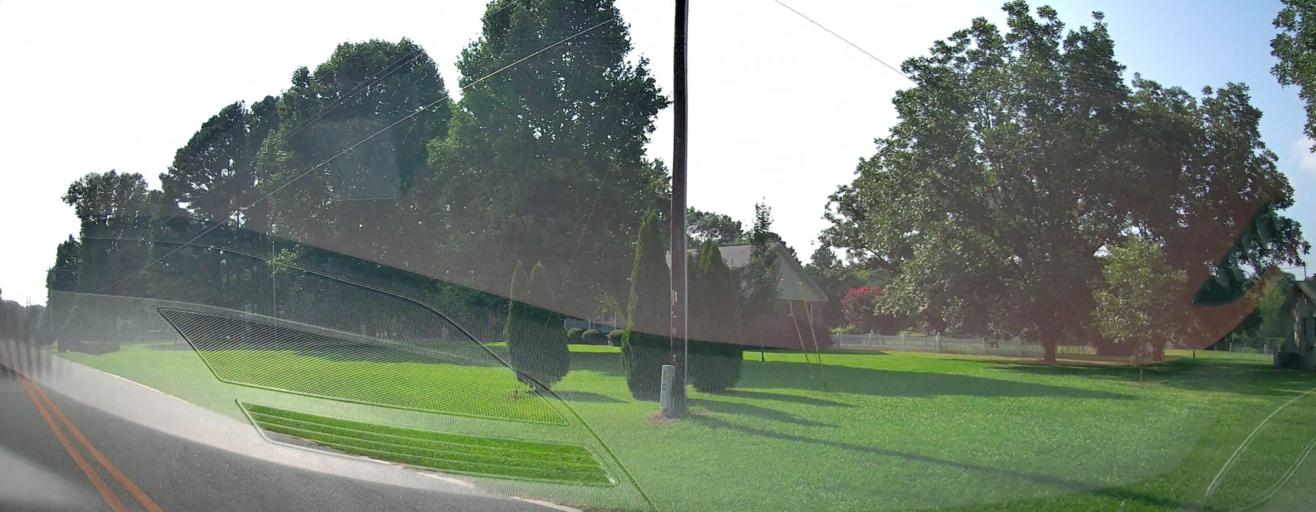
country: US
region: Georgia
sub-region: Houston County
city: Centerville
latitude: 32.6530
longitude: -83.6932
